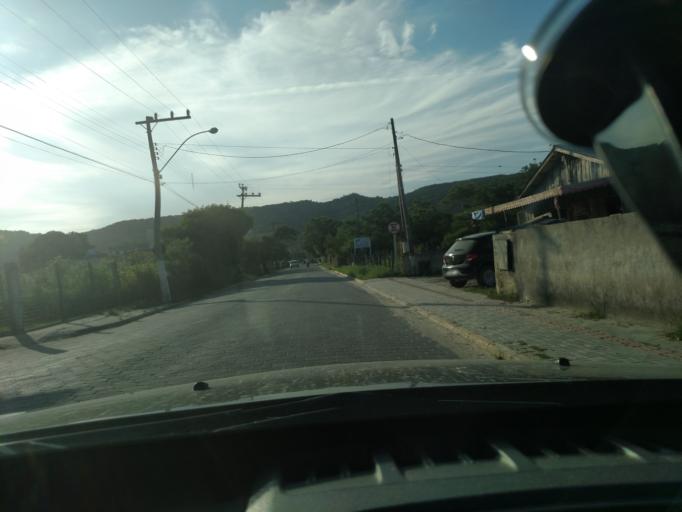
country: BR
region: Santa Catarina
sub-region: Porto Belo
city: Porto Belo
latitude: -27.1488
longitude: -48.5094
